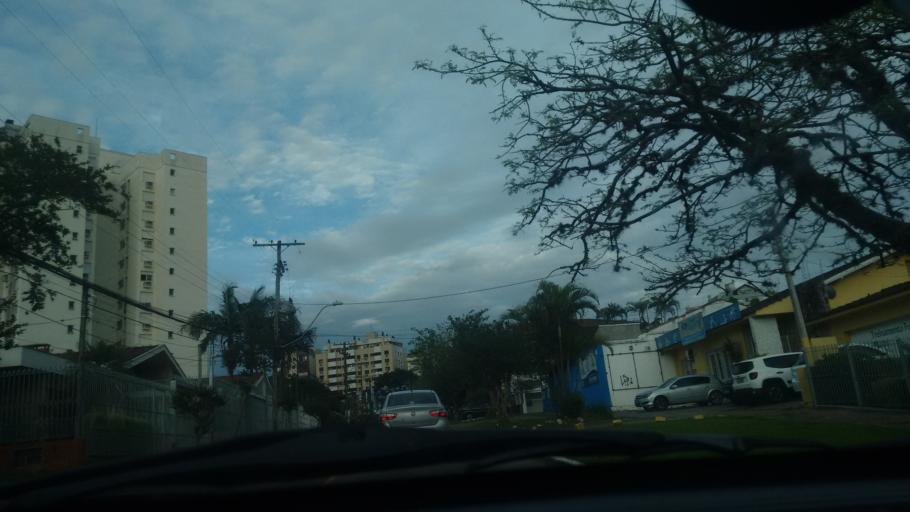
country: BR
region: Rio Grande do Sul
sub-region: Cachoeirinha
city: Cachoeirinha
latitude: -30.0060
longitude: -51.1526
